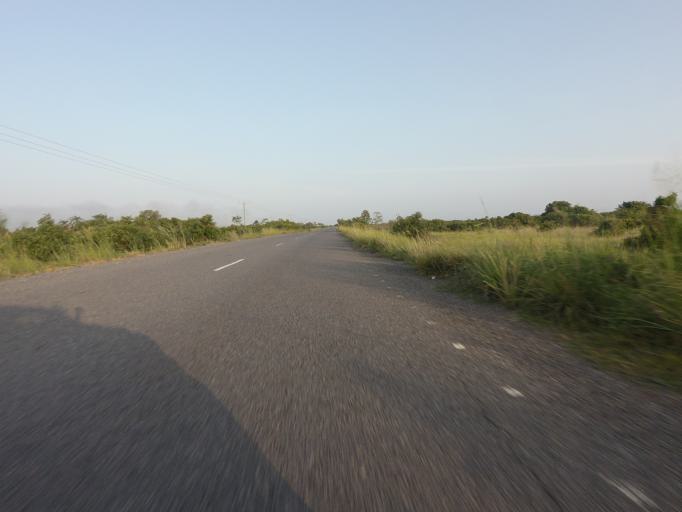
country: GH
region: Volta
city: Anloga
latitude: 5.8430
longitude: 0.7821
